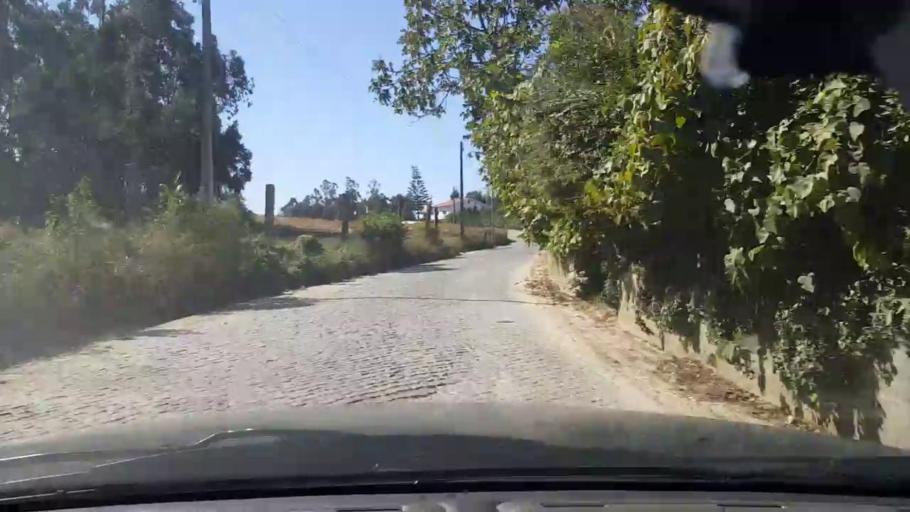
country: PT
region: Porto
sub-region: Maia
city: Gemunde
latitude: 41.2931
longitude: -8.6664
